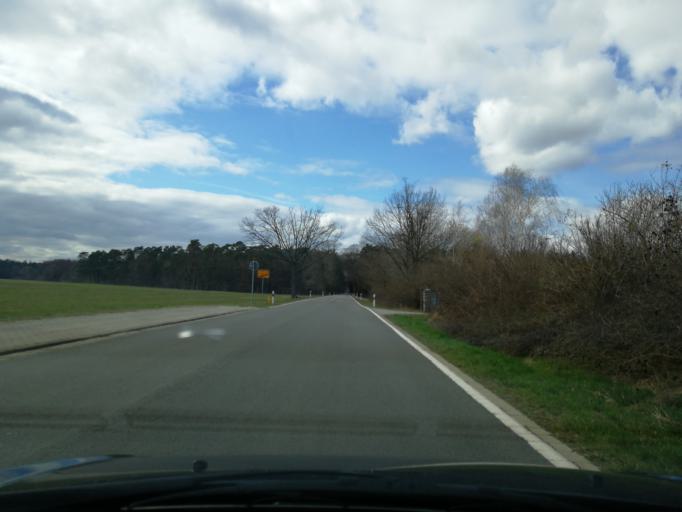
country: DE
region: Brandenburg
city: Altdobern
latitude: 51.7149
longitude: 14.0362
